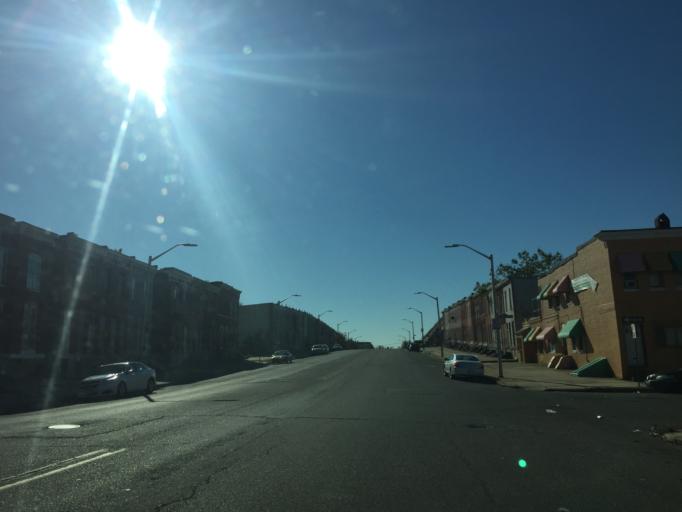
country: US
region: Maryland
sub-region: City of Baltimore
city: Baltimore
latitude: 39.3113
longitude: -76.5838
